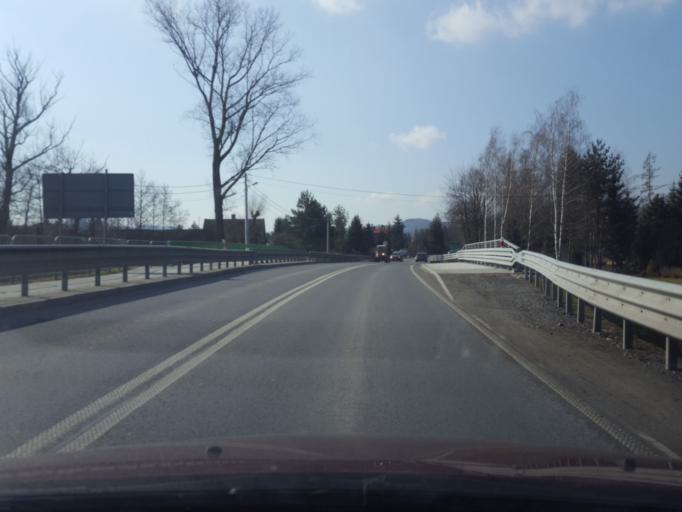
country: PL
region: Lesser Poland Voivodeship
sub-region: Powiat brzeski
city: Czchow
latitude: 49.8503
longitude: 20.6881
